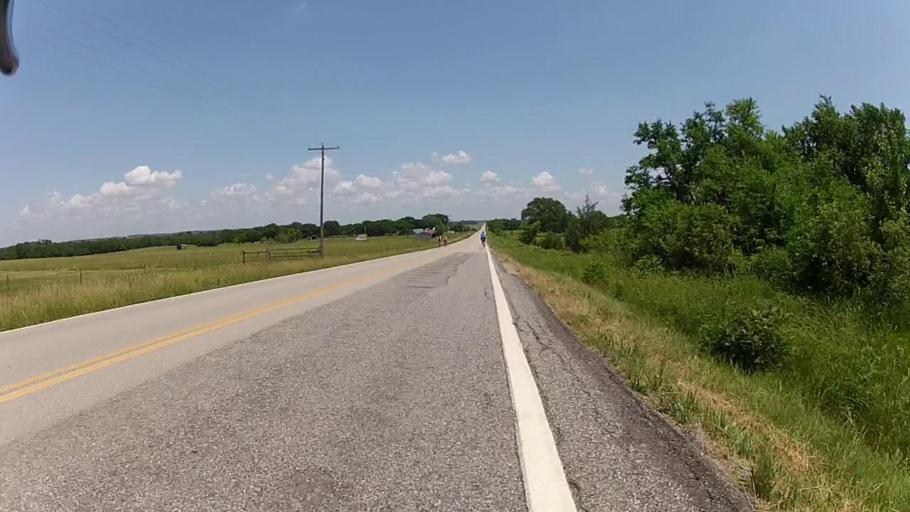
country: US
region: Kansas
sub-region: Montgomery County
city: Cherryvale
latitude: 37.1928
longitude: -95.4727
